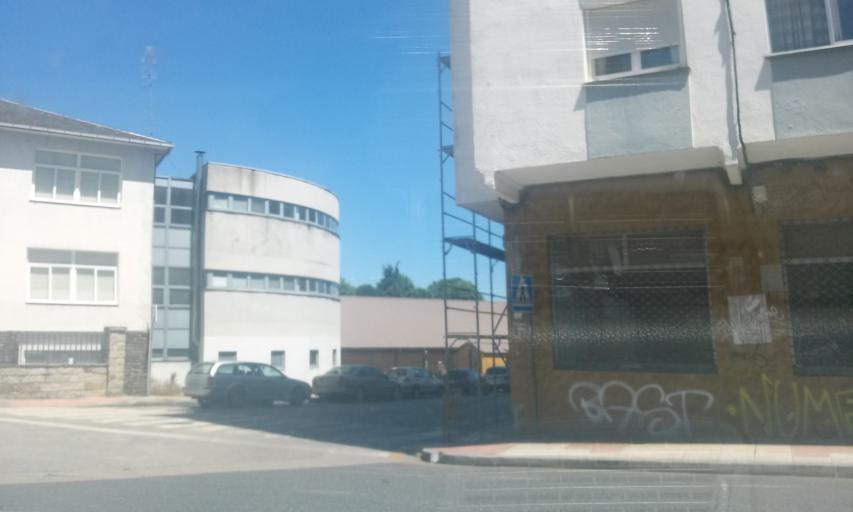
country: ES
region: Galicia
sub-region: Provincia de Lugo
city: Lugo
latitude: 43.0223
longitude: -7.5617
